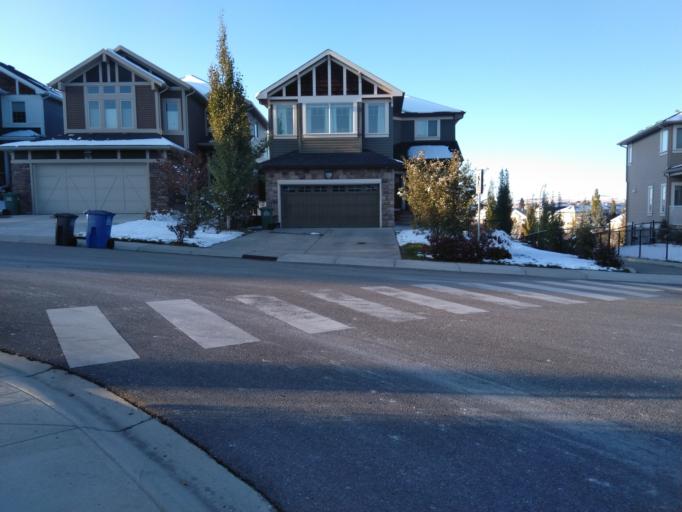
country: CA
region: Alberta
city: Cochrane
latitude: 51.1836
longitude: -114.5043
